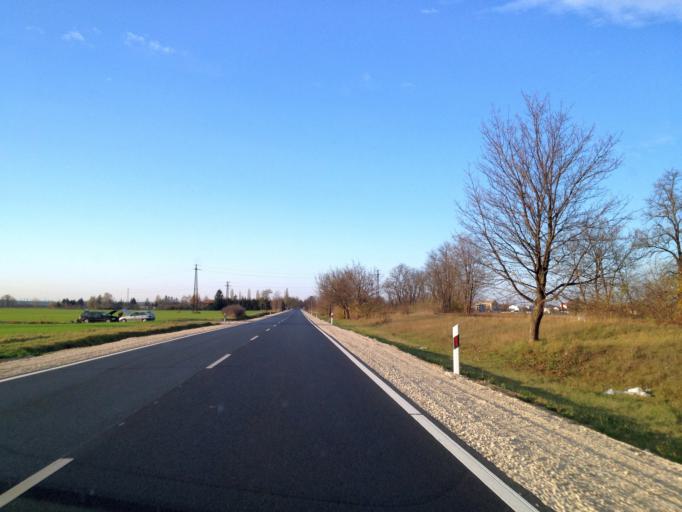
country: HU
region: Gyor-Moson-Sopron
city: Gyorujbarat
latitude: 47.6377
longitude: 17.6679
